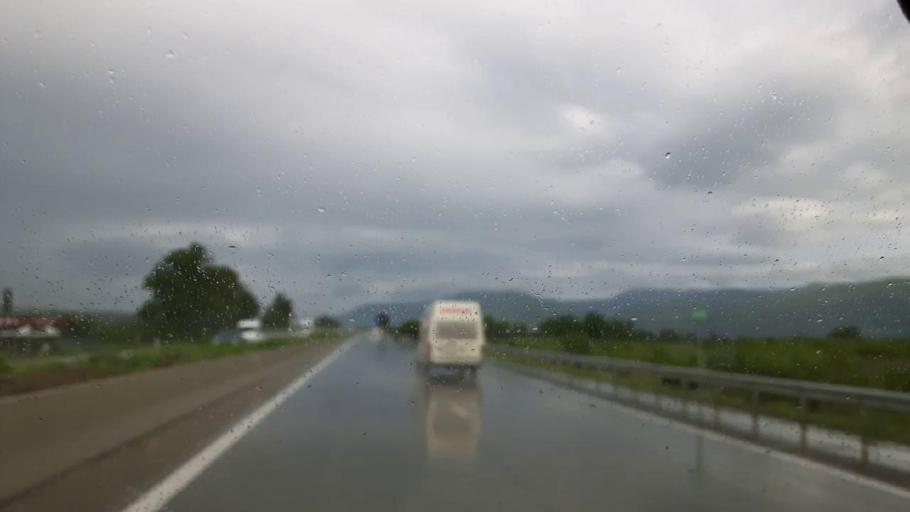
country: GE
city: Agara
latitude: 42.0357
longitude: 43.9401
